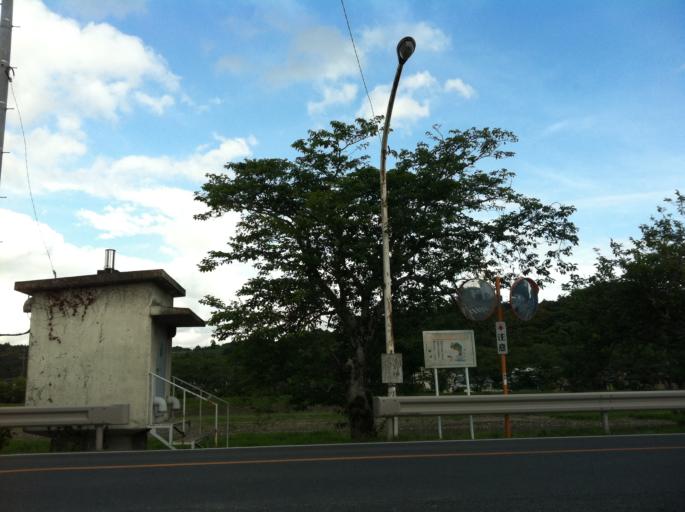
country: JP
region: Shizuoka
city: Mori
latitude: 34.8380
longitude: 137.9326
